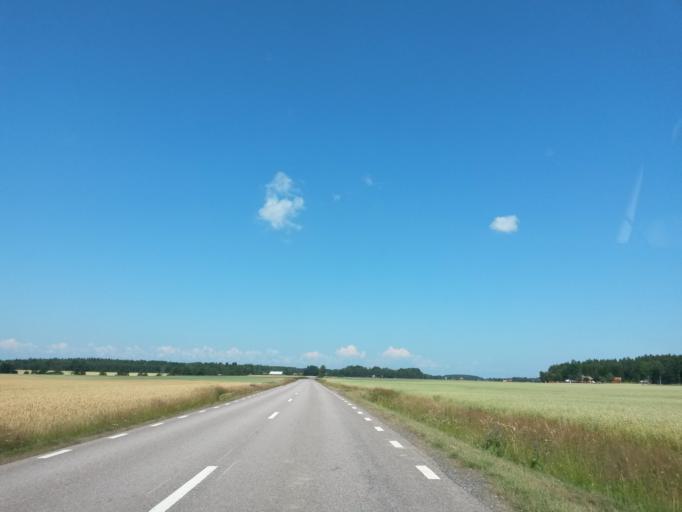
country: SE
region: Vaestra Goetaland
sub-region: Grastorps Kommun
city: Graestorp
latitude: 58.2821
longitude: 12.6741
